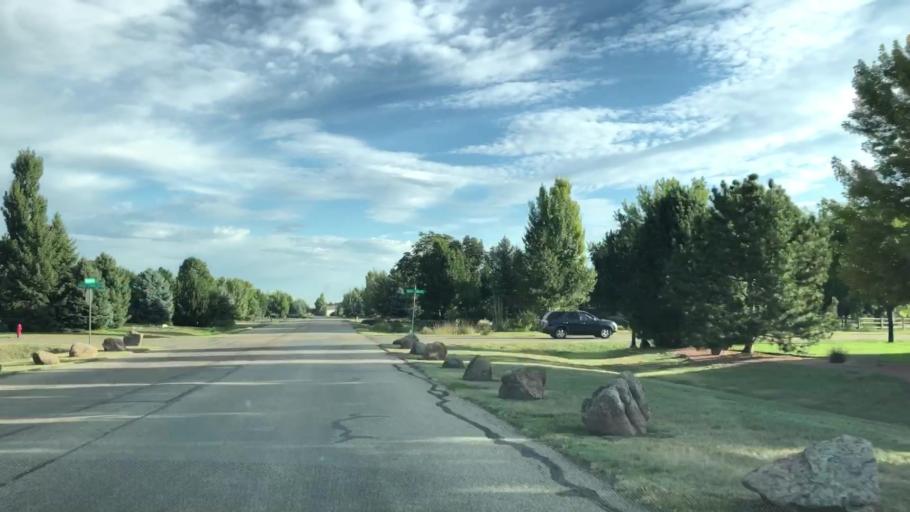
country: US
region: Colorado
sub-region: Weld County
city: Windsor
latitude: 40.4370
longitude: -104.9513
